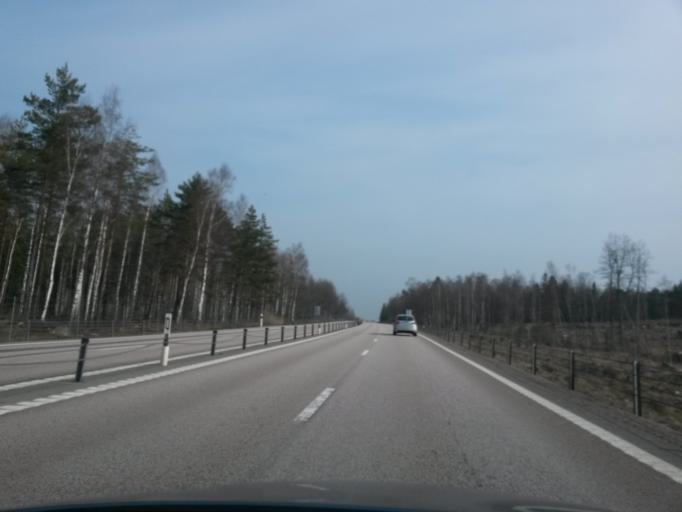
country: SE
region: Vaestra Goetaland
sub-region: Toreboda Kommun
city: Toereboda
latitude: 58.7681
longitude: 13.9870
